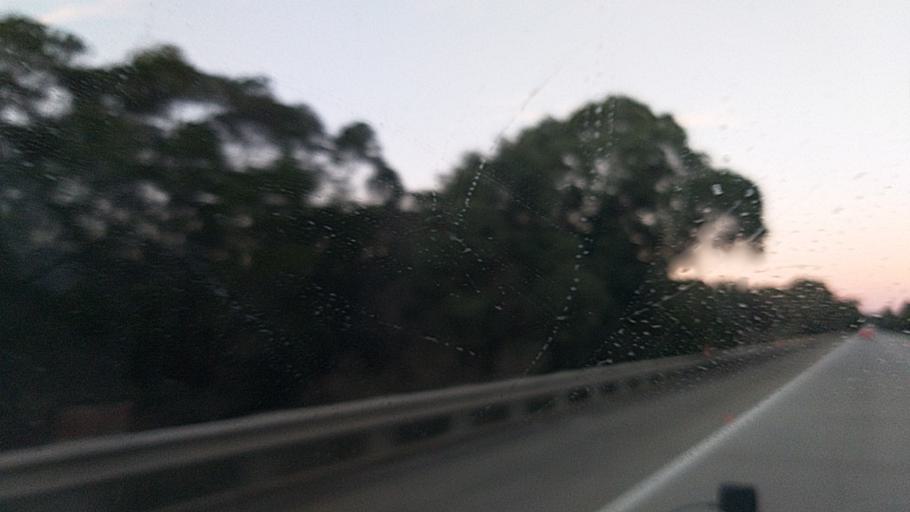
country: AU
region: New South Wales
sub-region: Wingecarribee
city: Bundanoon
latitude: -34.6842
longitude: 150.0501
